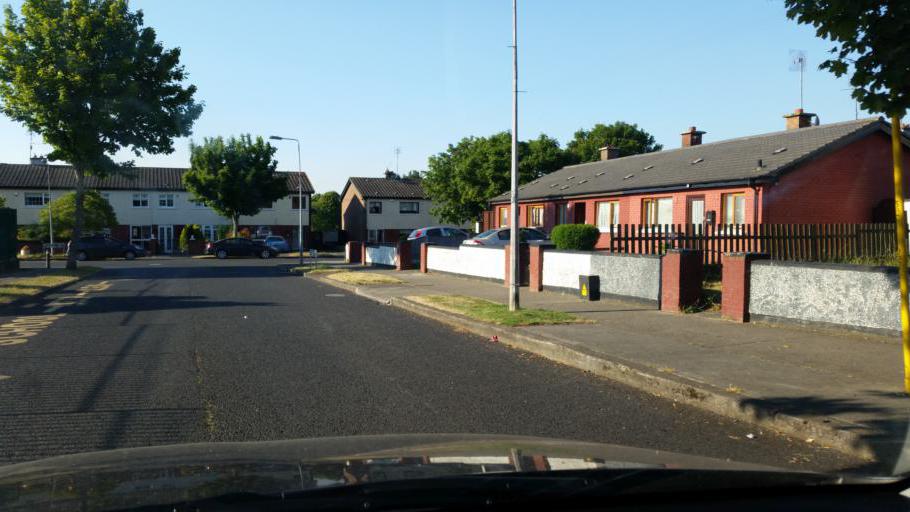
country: IE
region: Leinster
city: Ballymun
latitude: 53.4526
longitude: -6.2917
